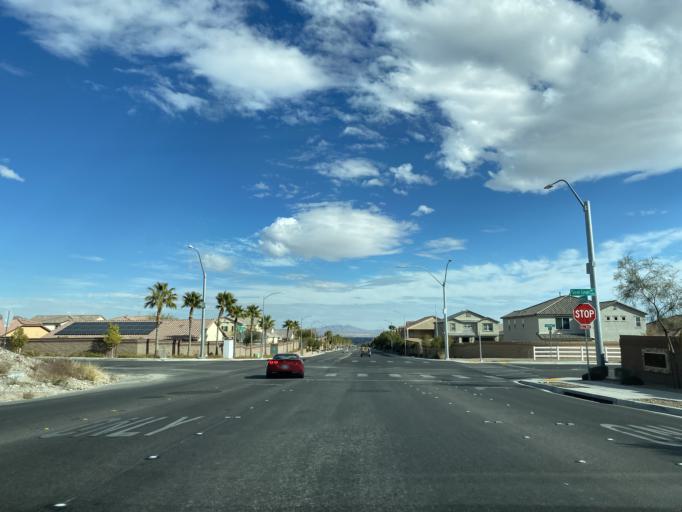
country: US
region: Nevada
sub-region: Clark County
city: Summerlin South
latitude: 36.2846
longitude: -115.3064
